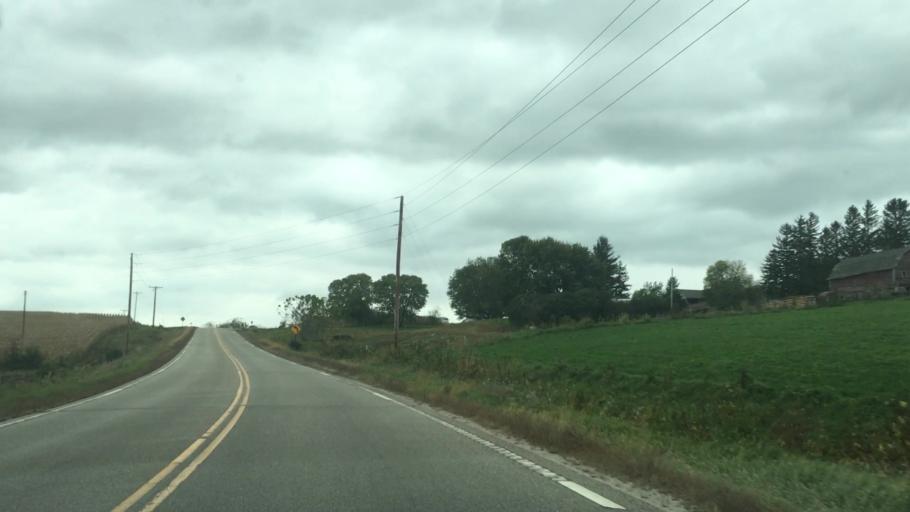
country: US
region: Minnesota
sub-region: Fillmore County
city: Preston
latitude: 43.7355
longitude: -92.0236
